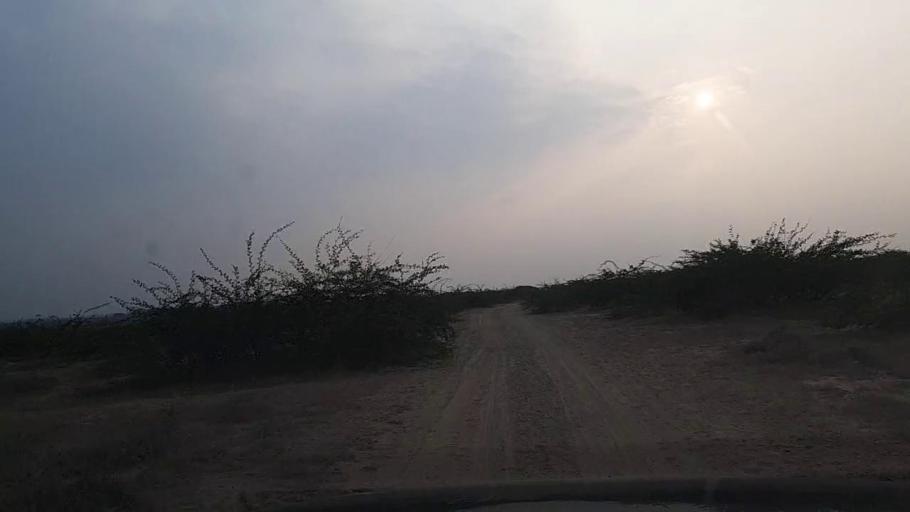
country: PK
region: Sindh
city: Gharo
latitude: 24.7725
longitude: 67.6943
